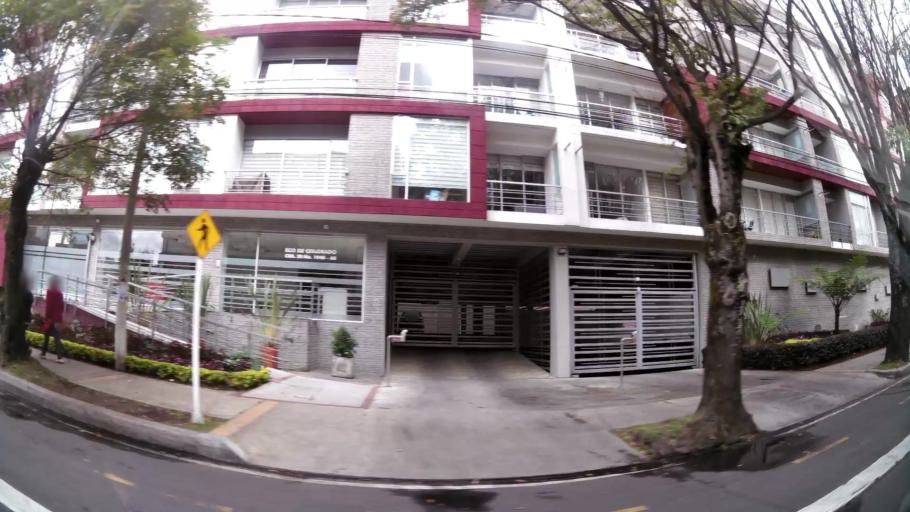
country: CO
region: Bogota D.C.
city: Barrio San Luis
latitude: 4.6944
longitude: -74.0607
